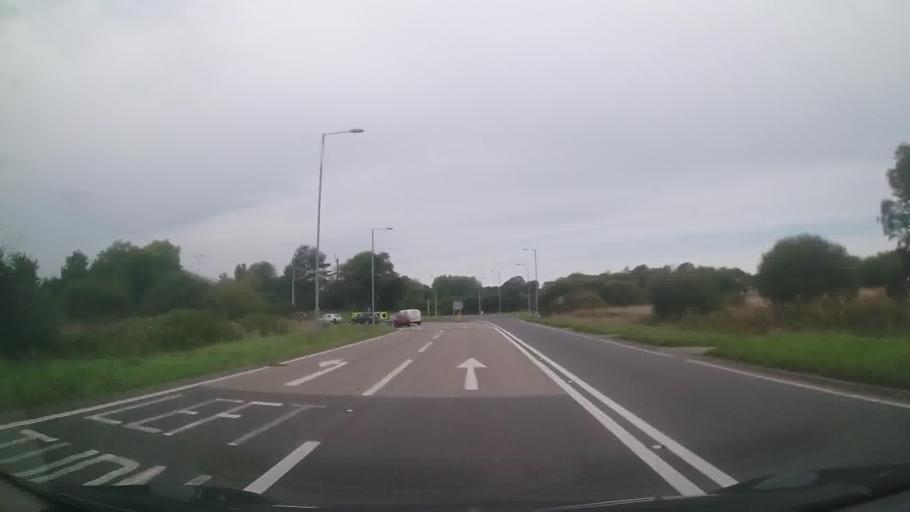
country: GB
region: Wales
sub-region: Pembrokeshire
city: Kilgetty
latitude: 51.7290
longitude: -4.7202
